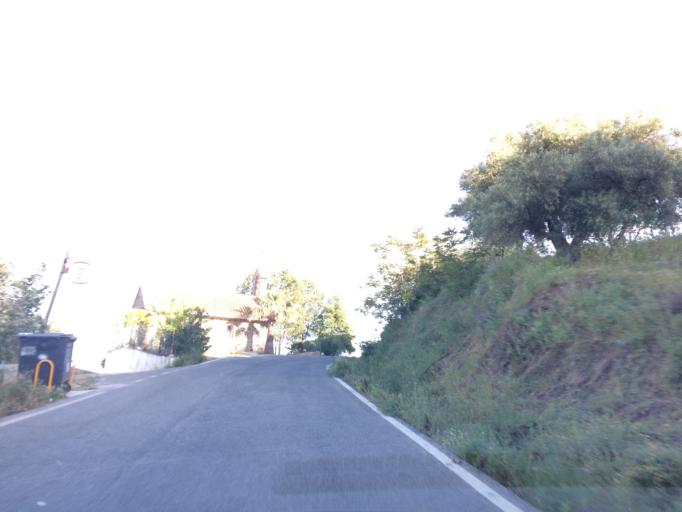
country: ES
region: Andalusia
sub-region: Provincia de Malaga
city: Totalan
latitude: 36.7678
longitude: -4.3208
